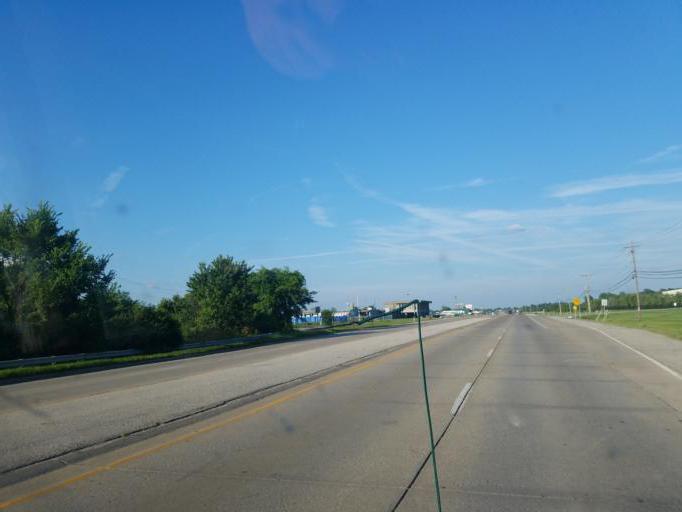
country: US
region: Kentucky
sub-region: Jefferson County
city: Heritage Creek
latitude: 38.1302
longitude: -85.7357
